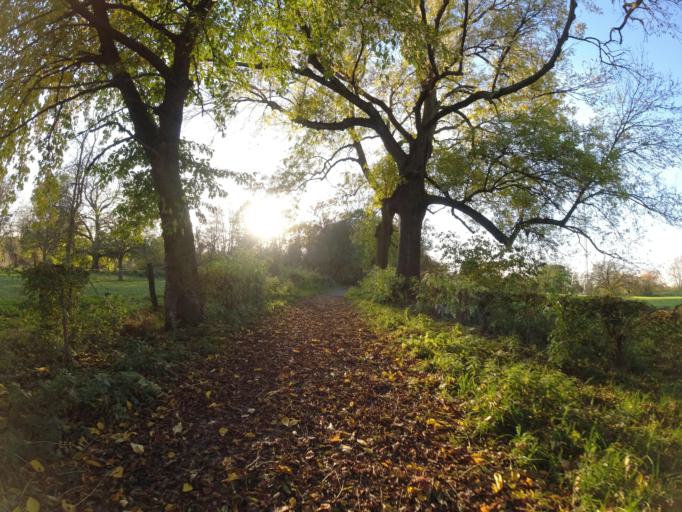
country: DE
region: North Rhine-Westphalia
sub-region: Regierungsbezirk Dusseldorf
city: Hochfeld
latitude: 51.3789
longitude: 6.6997
